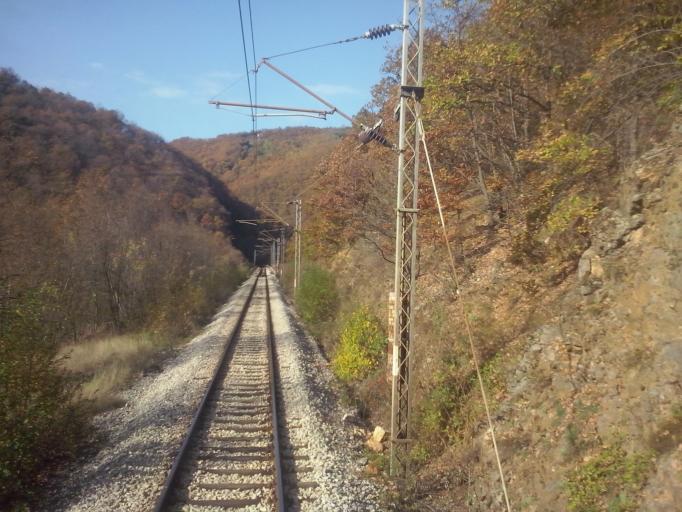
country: RS
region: Central Serbia
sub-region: Kolubarski Okrug
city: Valjevo
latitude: 44.2330
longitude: 19.8702
